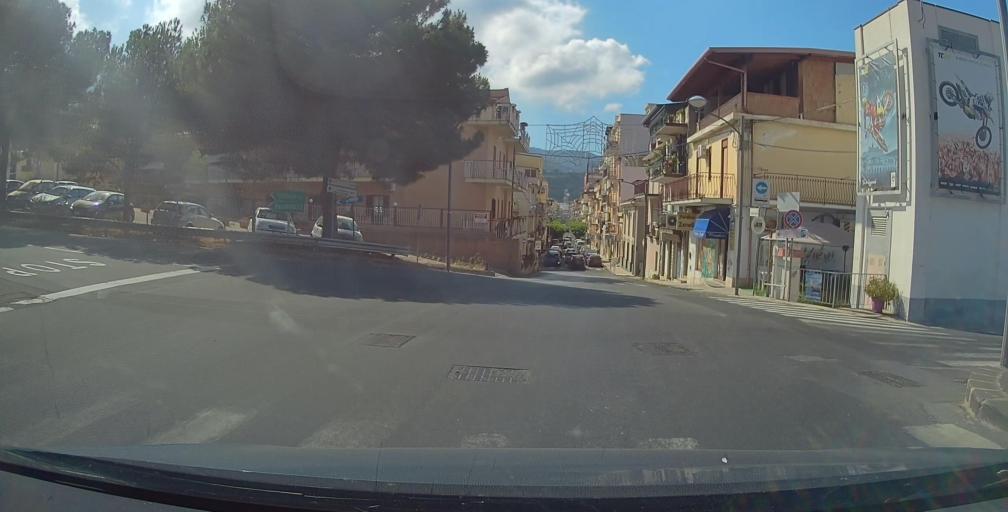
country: IT
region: Sicily
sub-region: Messina
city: Patti
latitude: 38.1509
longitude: 14.9718
